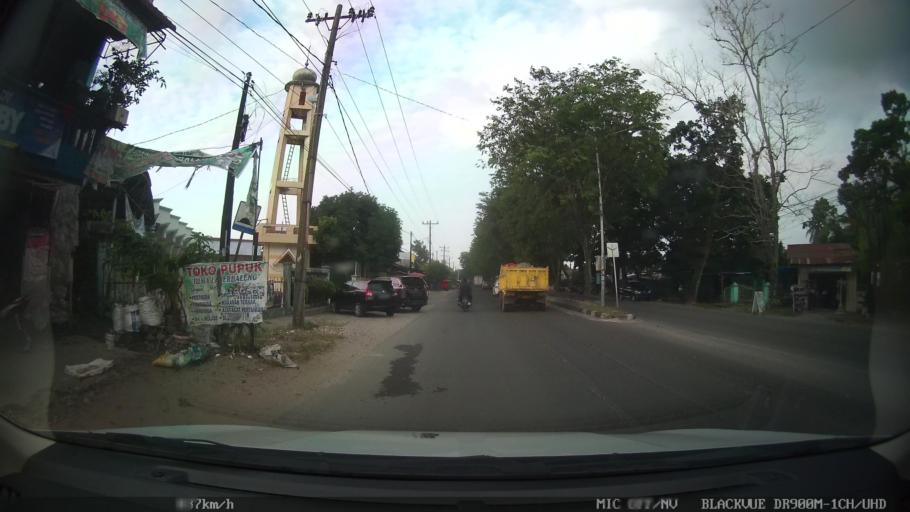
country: ID
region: North Sumatra
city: Sunggal
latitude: 3.5482
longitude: 98.6070
